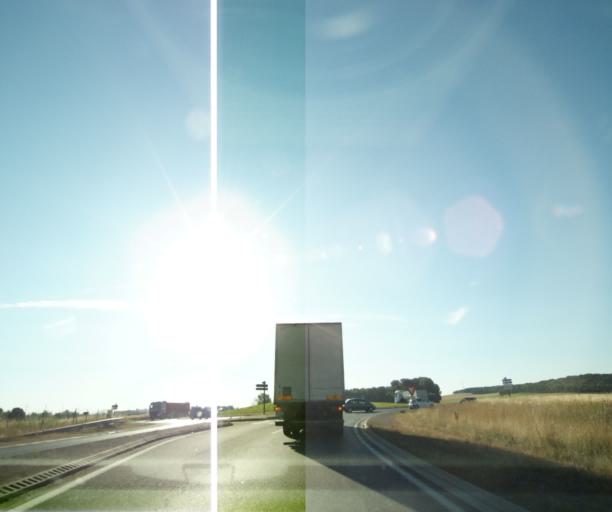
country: FR
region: Ile-de-France
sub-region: Departement de Seine-et-Marne
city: Varennes-sur-Seine
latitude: 48.3609
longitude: 2.9290
